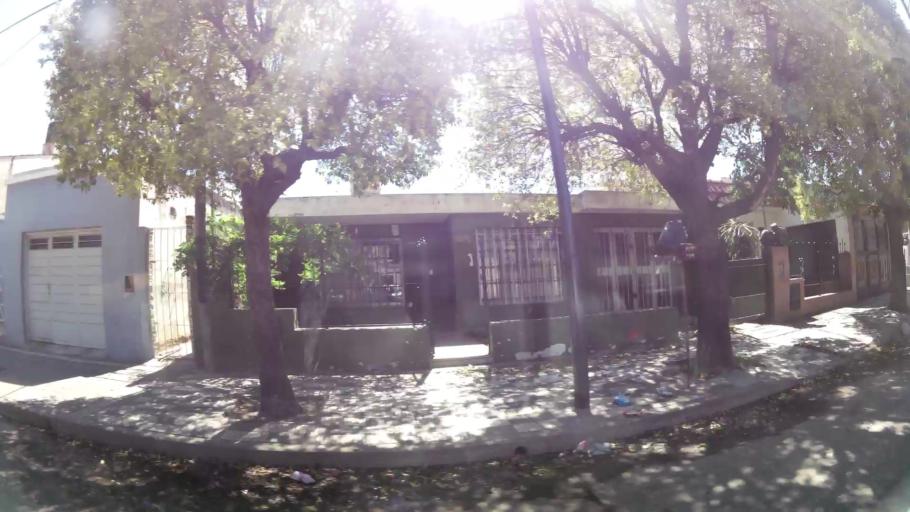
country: AR
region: Cordoba
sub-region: Departamento de Capital
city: Cordoba
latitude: -31.3670
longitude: -64.1382
